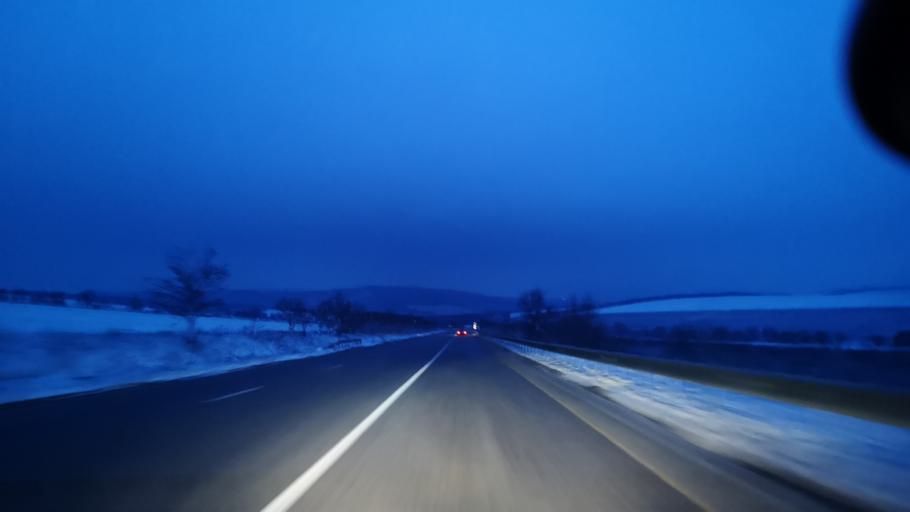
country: MD
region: Orhei
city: Orhei
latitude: 47.5294
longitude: 28.7953
